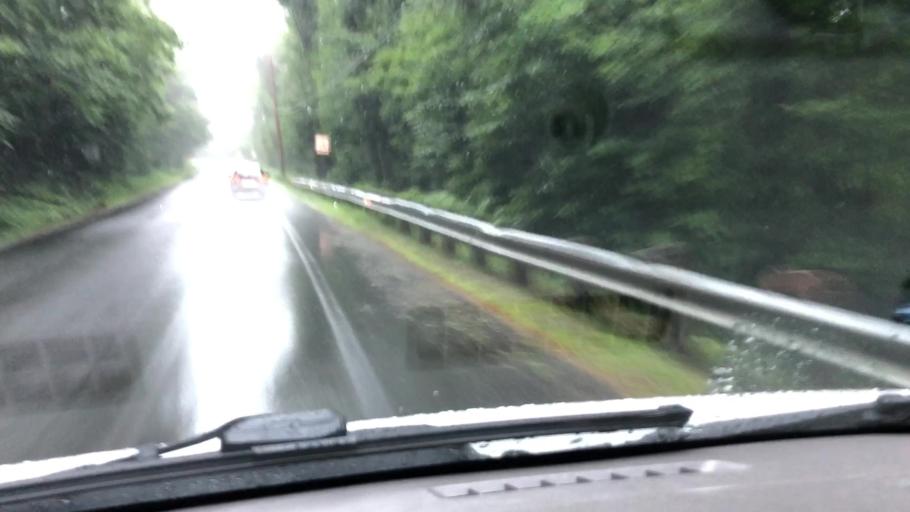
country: US
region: Massachusetts
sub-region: Hampshire County
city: Chesterfield
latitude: 42.4476
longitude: -72.9771
